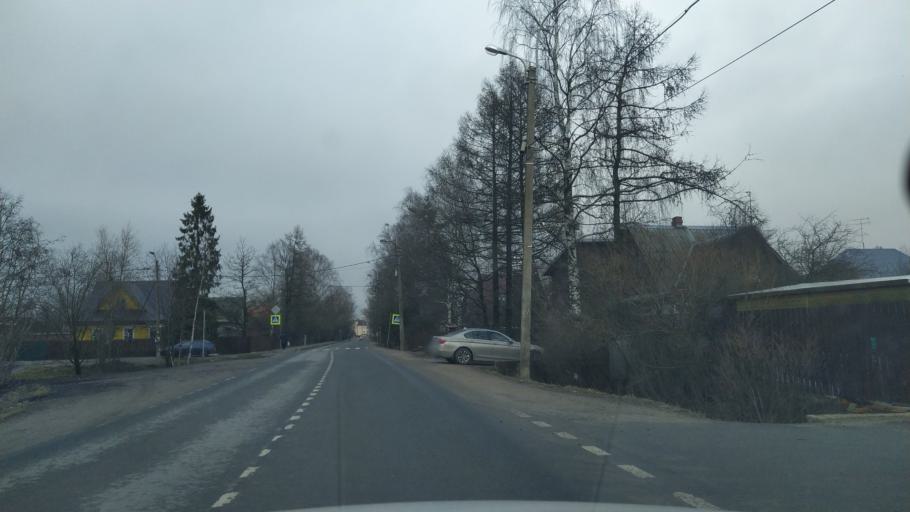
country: RU
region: St.-Petersburg
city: Aleksandrovskaya
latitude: 59.7257
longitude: 30.3514
